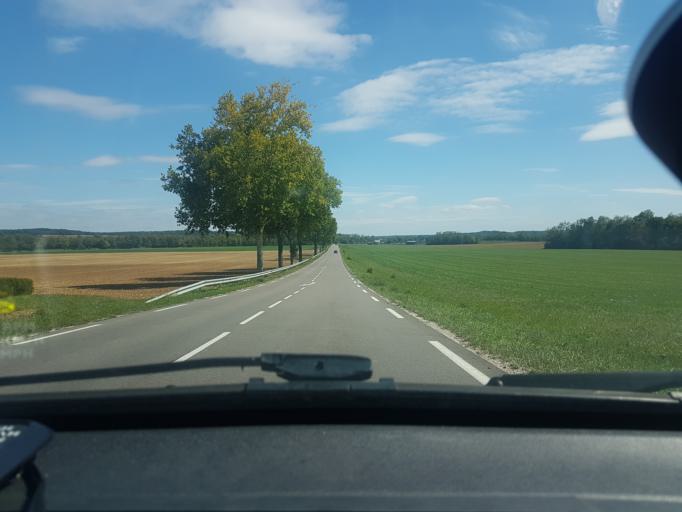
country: FR
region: Bourgogne
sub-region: Departement de la Cote-d'Or
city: Mirebeau-sur-Beze
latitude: 47.4037
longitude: 5.3859
